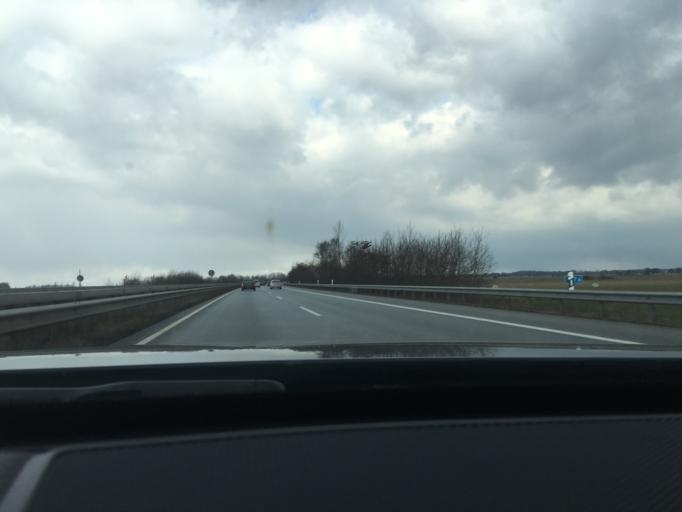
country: DE
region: Lower Saxony
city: Driftsethe
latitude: 53.3801
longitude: 8.5746
